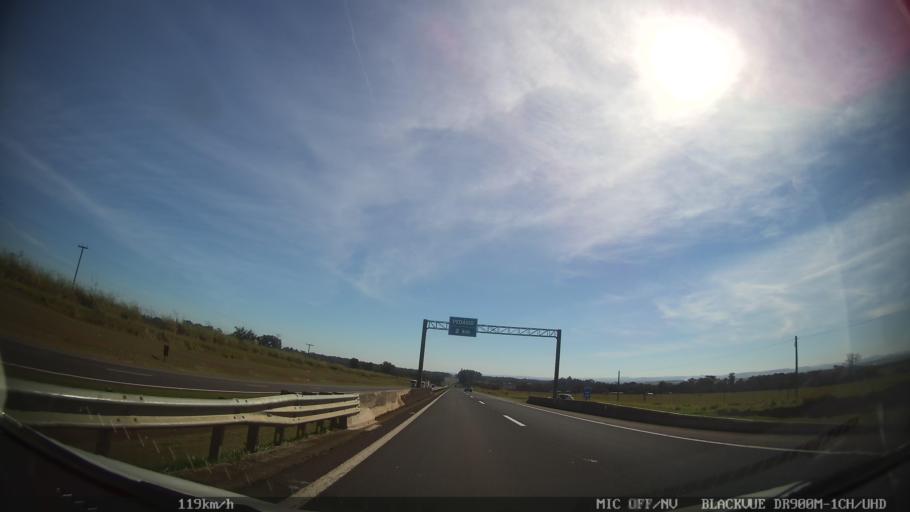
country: BR
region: Sao Paulo
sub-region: Pirassununga
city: Pirassununga
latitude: -21.9750
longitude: -47.4536
